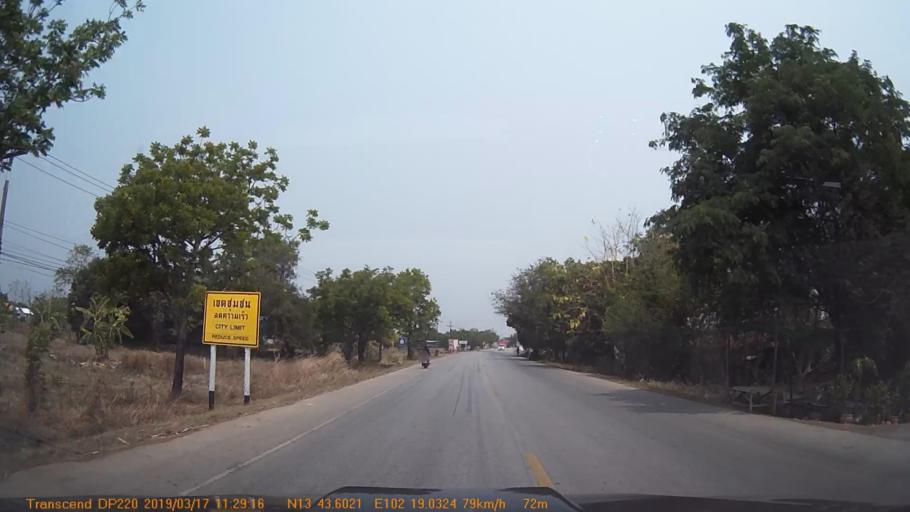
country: TH
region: Sa Kaeo
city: Watthana Nakhon
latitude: 13.7270
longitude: 102.3173
